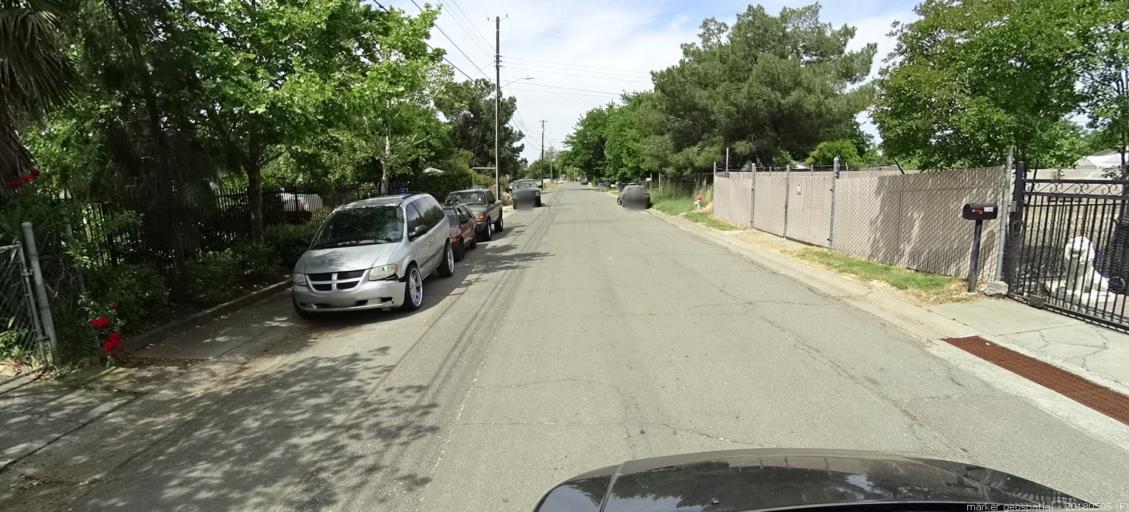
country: US
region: California
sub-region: Sacramento County
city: Arden-Arcade
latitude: 38.6454
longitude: -121.4127
